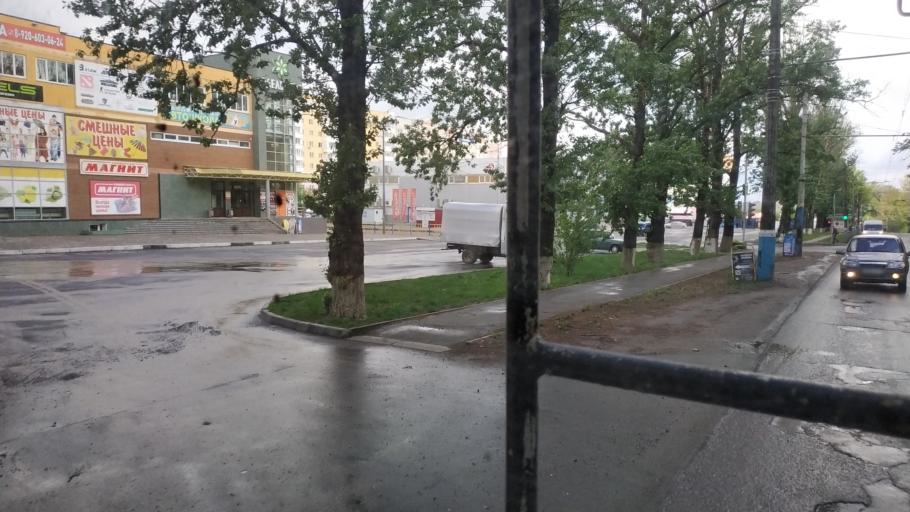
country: RU
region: Brjansk
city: Putevka
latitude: 53.2629
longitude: 34.3241
